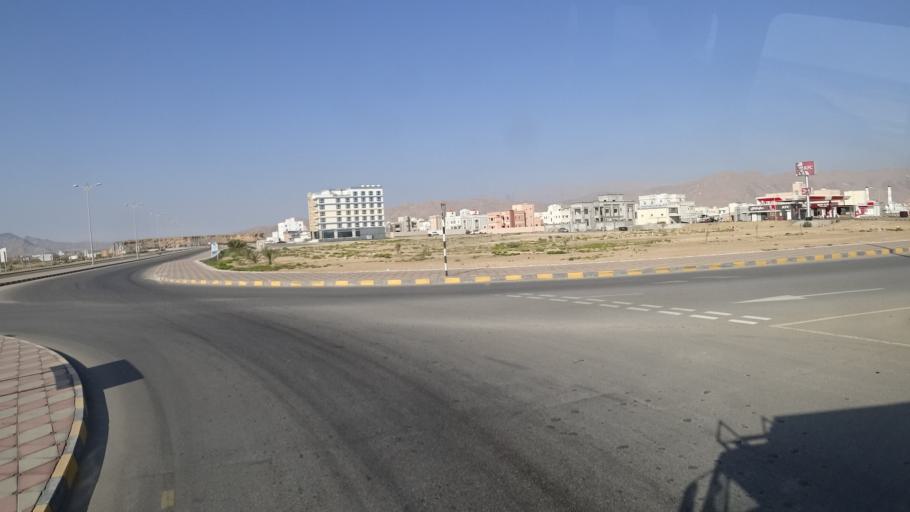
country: OM
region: Ash Sharqiyah
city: Sur
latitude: 22.6028
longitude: 59.4831
